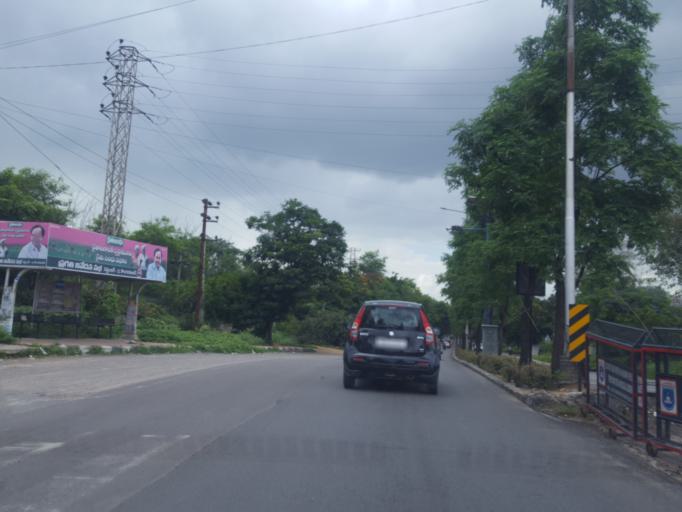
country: IN
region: Telangana
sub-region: Medak
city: Serilingampalle
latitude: 17.4577
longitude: 78.3397
